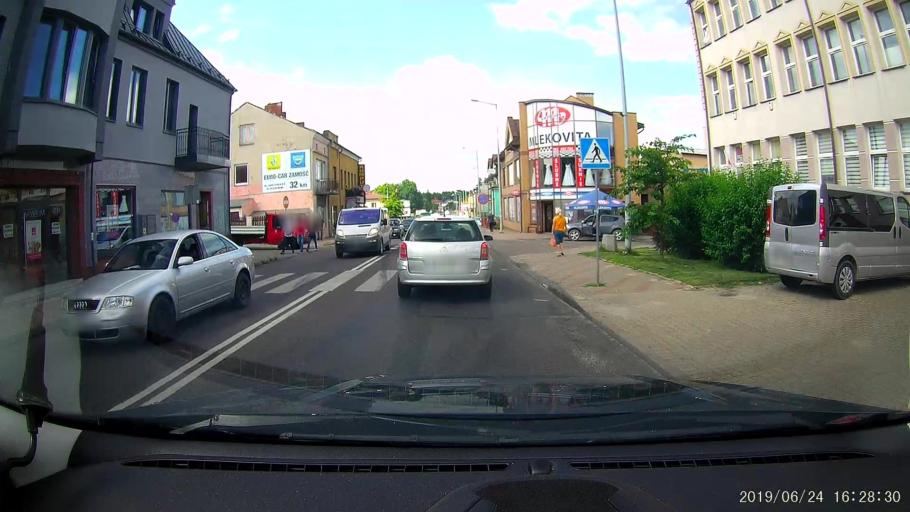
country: PL
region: Lublin Voivodeship
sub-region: Powiat tomaszowski
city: Tomaszow Lubelski
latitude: 50.4541
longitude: 23.4196
